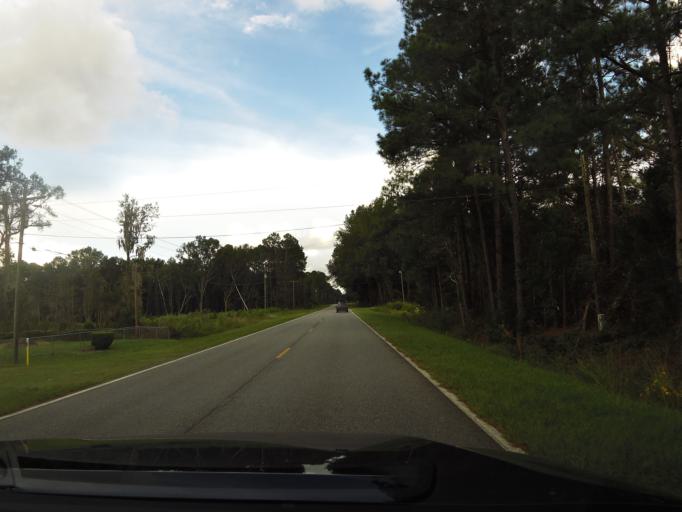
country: US
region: Georgia
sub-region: Liberty County
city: Midway
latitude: 31.8502
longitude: -81.4212
